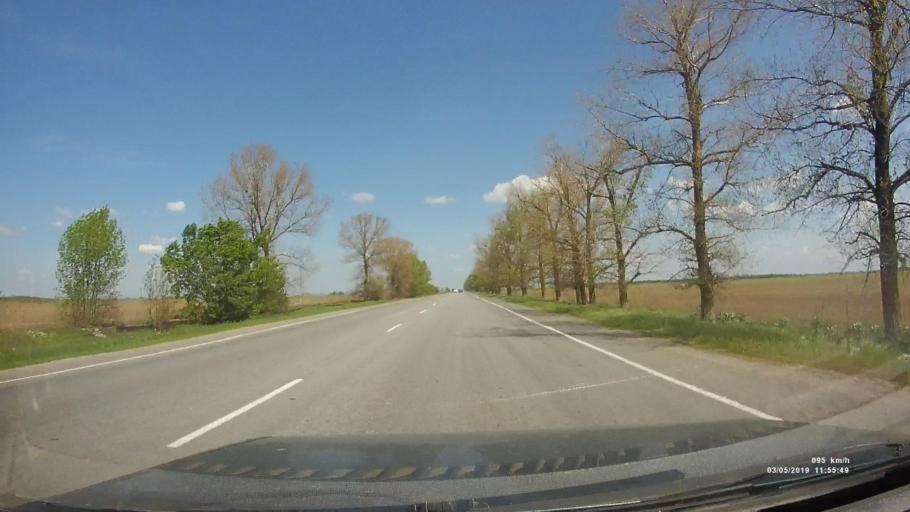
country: RU
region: Rostov
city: Bagayevskaya
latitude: 47.1859
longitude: 40.2946
